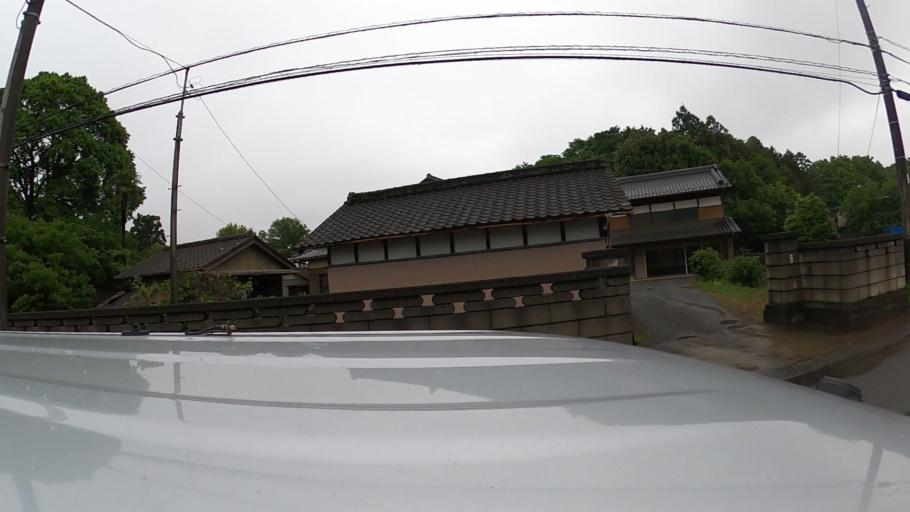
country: JP
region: Ibaraki
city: Ushiku
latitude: 36.0127
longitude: 140.1037
